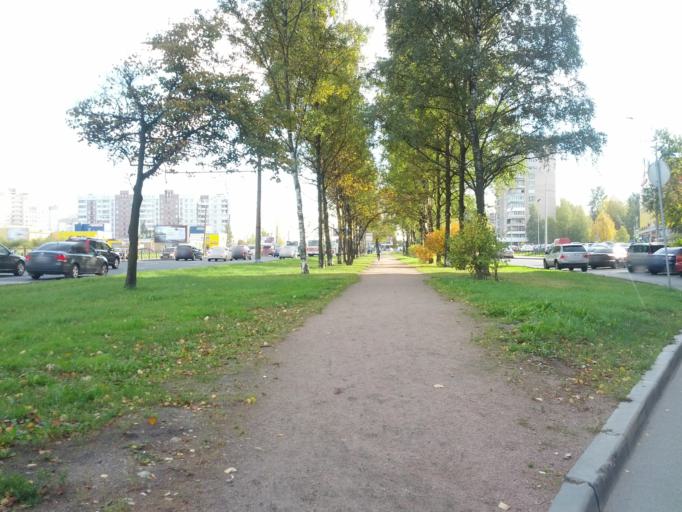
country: RU
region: Leningrad
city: Rybatskoye
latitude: 59.9020
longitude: 30.4867
